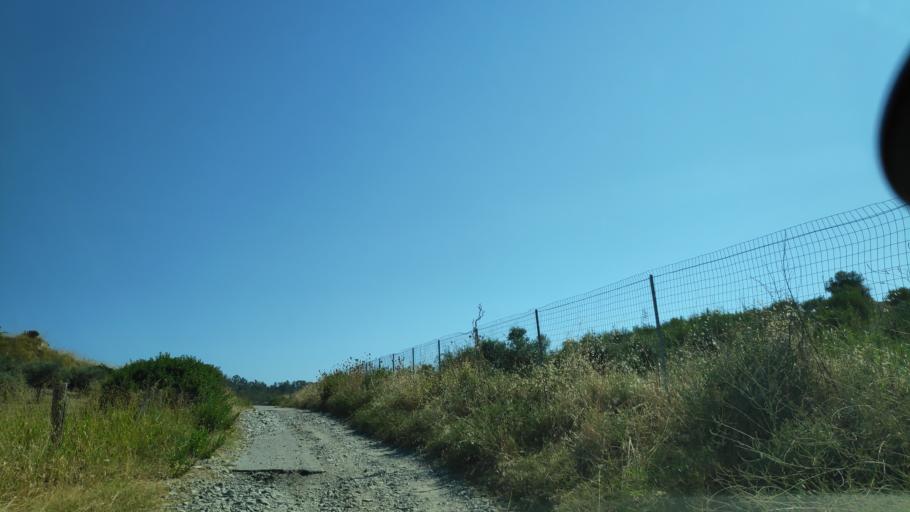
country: IT
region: Calabria
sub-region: Provincia di Reggio Calabria
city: Monasterace
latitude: 38.4331
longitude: 16.5249
